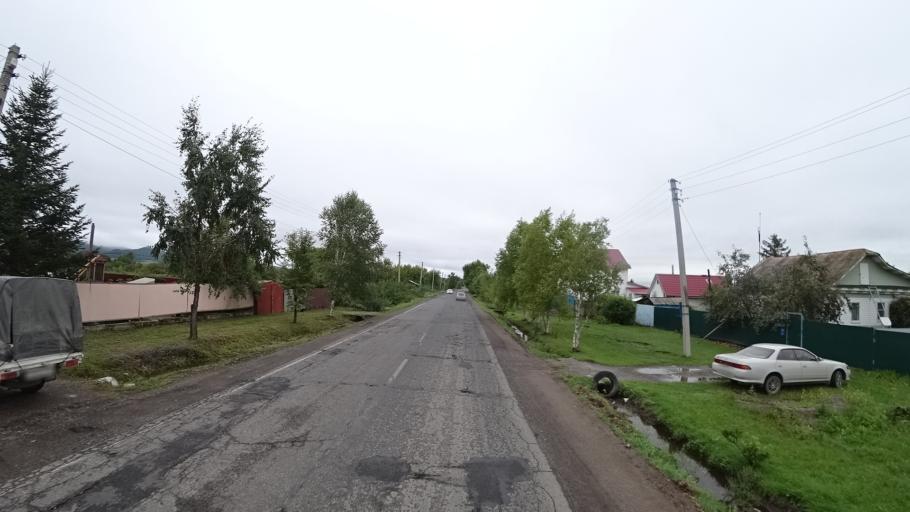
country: RU
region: Primorskiy
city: Monastyrishche
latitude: 44.1917
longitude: 132.4879
